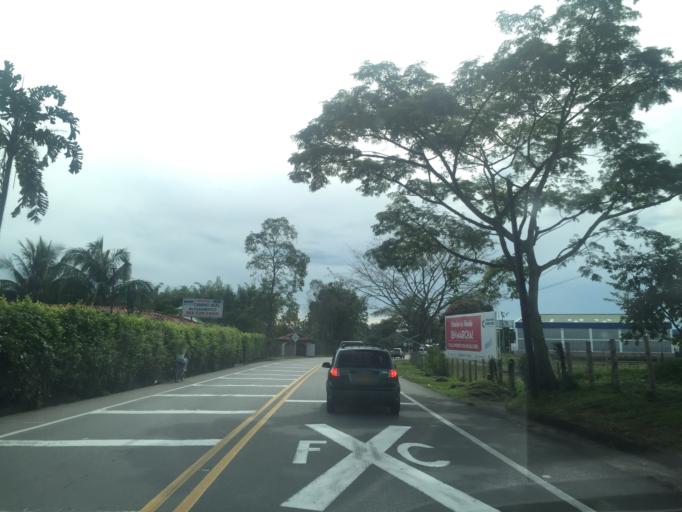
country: CO
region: Quindio
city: La Tebaida
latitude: 4.4635
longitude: -75.7795
